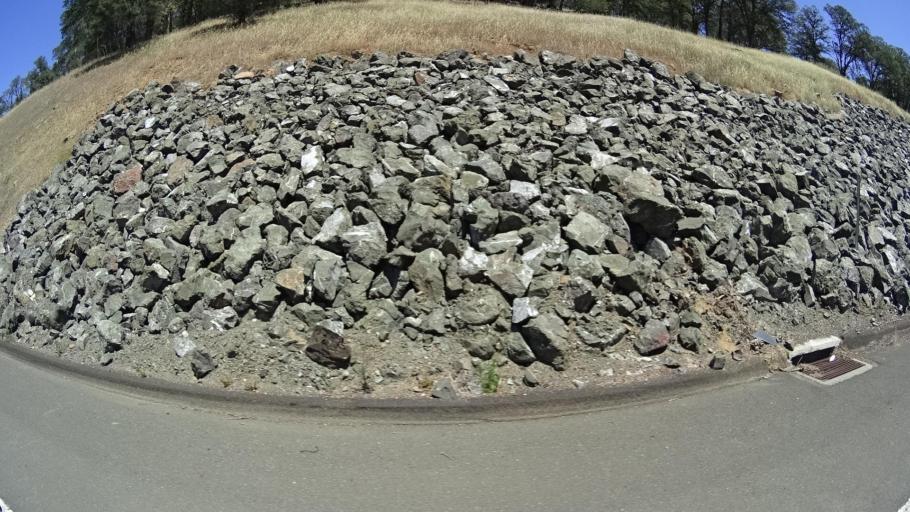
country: US
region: California
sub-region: Lake County
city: Hidden Valley Lake
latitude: 38.8209
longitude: -122.5775
